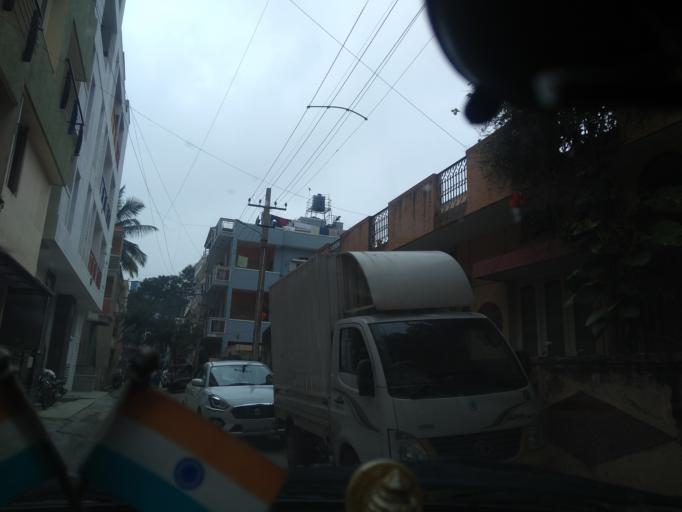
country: IN
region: Karnataka
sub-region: Bangalore Urban
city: Bangalore
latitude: 13.0088
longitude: 77.5575
